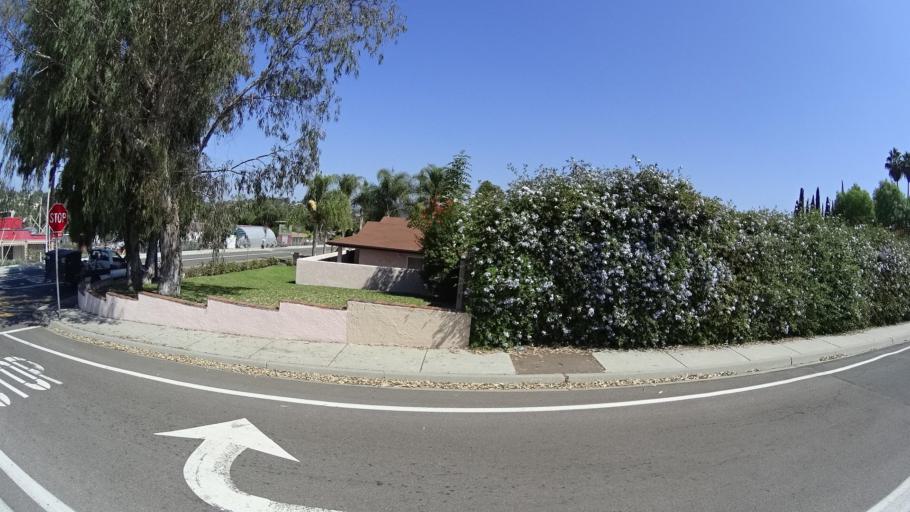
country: US
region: California
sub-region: San Diego County
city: Lake San Marcos
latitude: 33.1537
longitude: -117.2089
